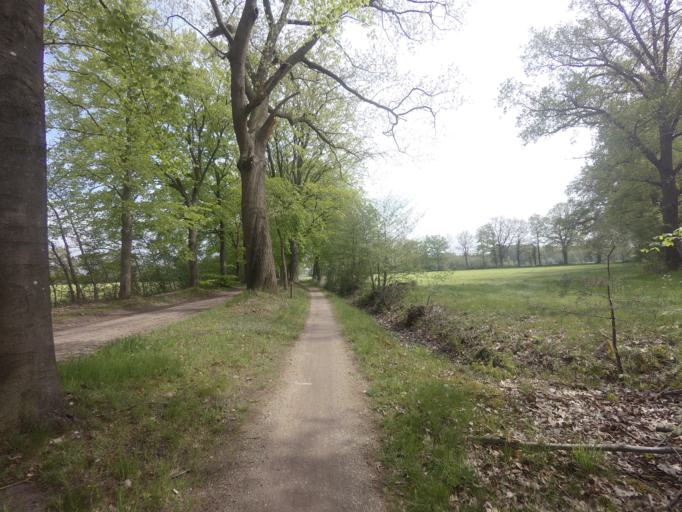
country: NL
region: Overijssel
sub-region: Gemeente Hof van Twente
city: Delden
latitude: 52.2657
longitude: 6.6864
